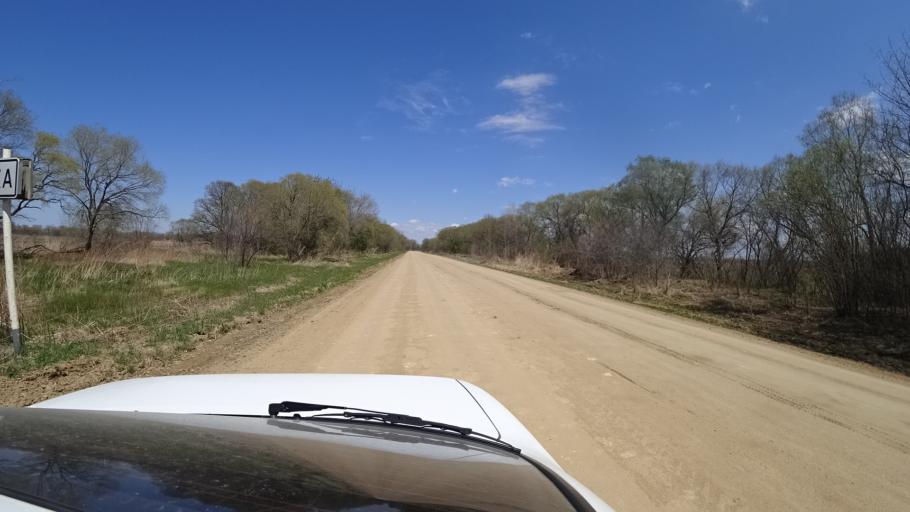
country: RU
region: Primorskiy
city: Dal'nerechensk
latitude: 45.8016
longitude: 133.7736
